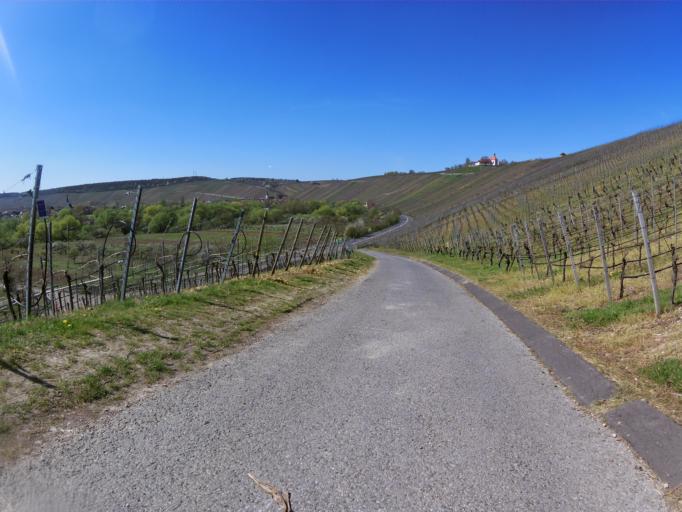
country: DE
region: Bavaria
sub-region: Regierungsbezirk Unterfranken
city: Nordheim
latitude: 49.8654
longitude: 10.1948
